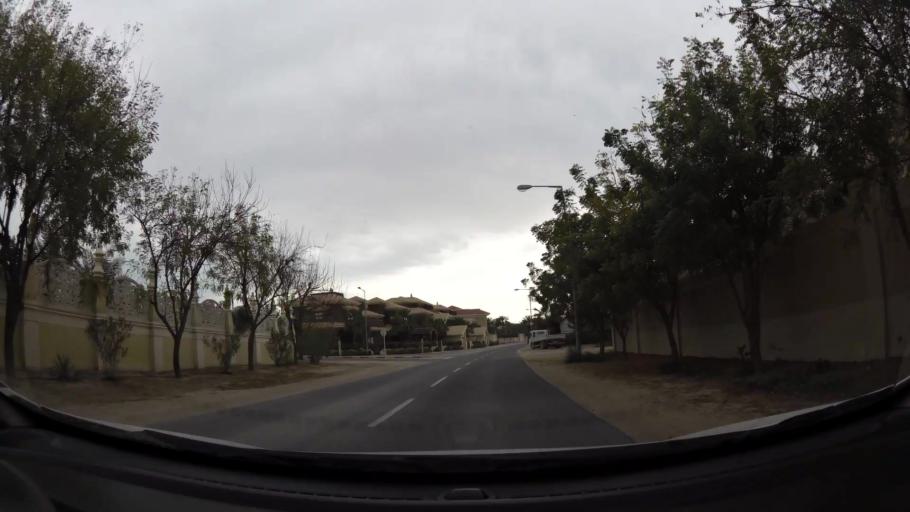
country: BH
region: Central Governorate
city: Madinat Hamad
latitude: 26.1495
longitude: 50.4719
